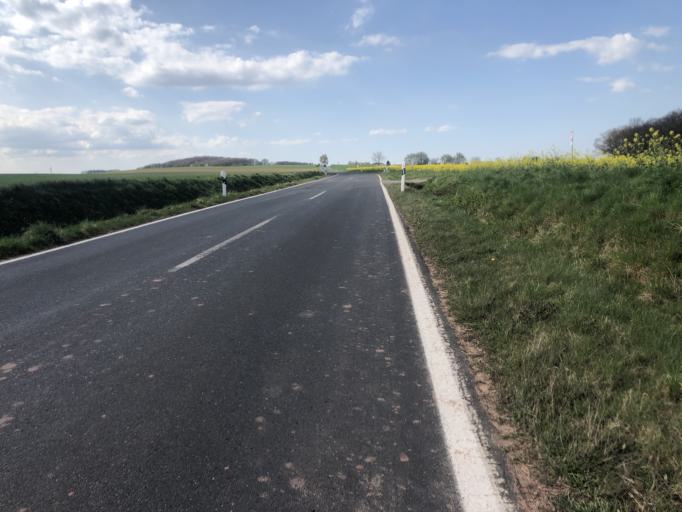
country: DE
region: North Rhine-Westphalia
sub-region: Regierungsbezirk Koln
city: Kall
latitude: 50.6084
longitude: 6.5766
